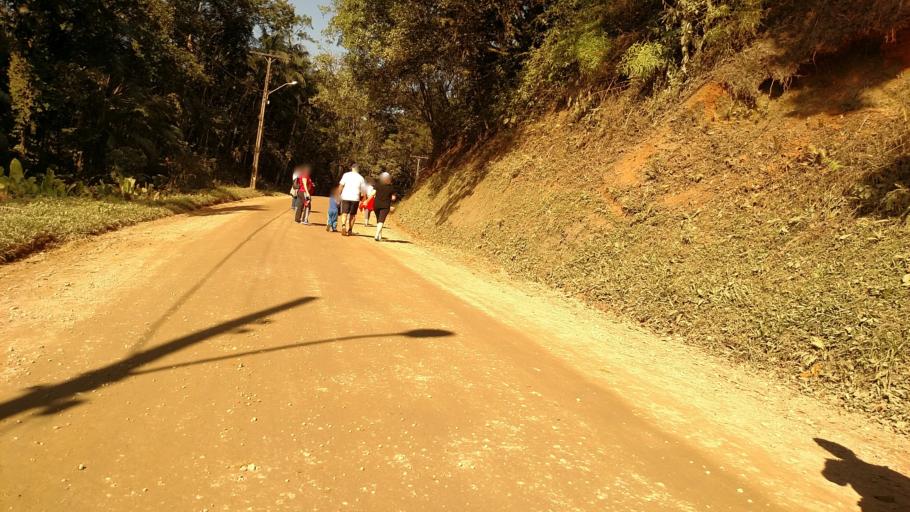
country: BR
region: Santa Catarina
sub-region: Pomerode
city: Pomerode
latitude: -26.7343
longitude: -49.0728
